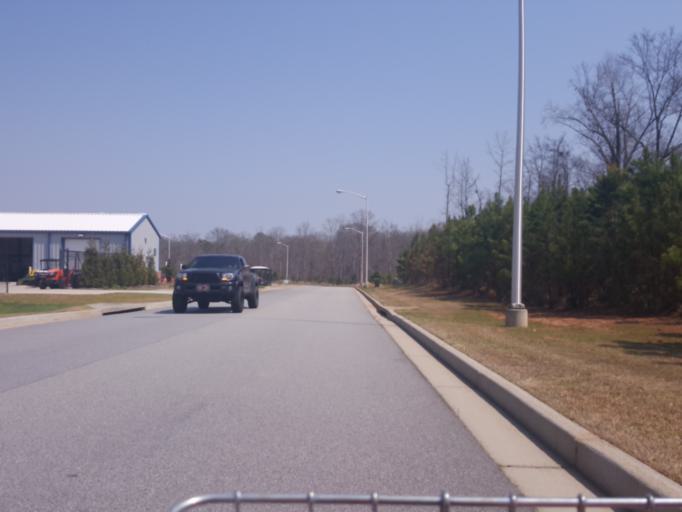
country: US
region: Georgia
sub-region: Carroll County
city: Carrollton
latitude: 33.5758
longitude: -85.1187
